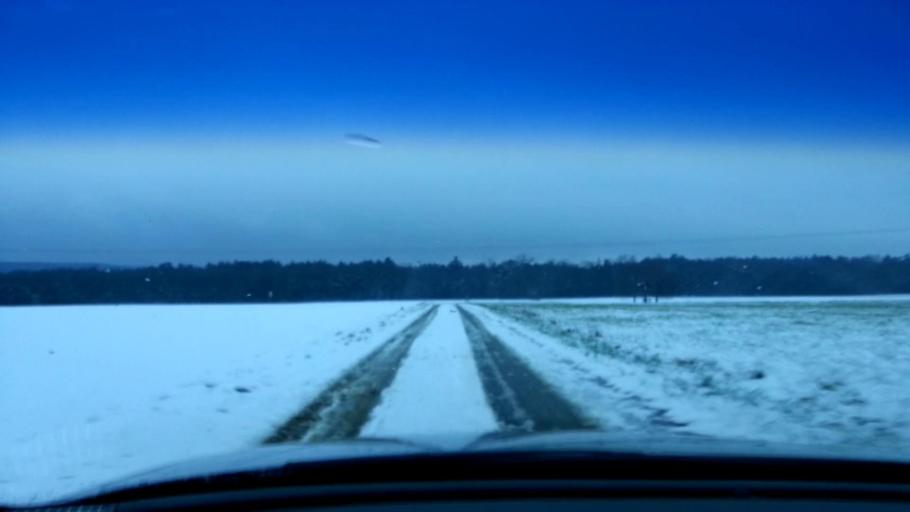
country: DE
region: Bavaria
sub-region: Upper Franconia
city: Litzendorf
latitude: 49.9220
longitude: 10.9882
